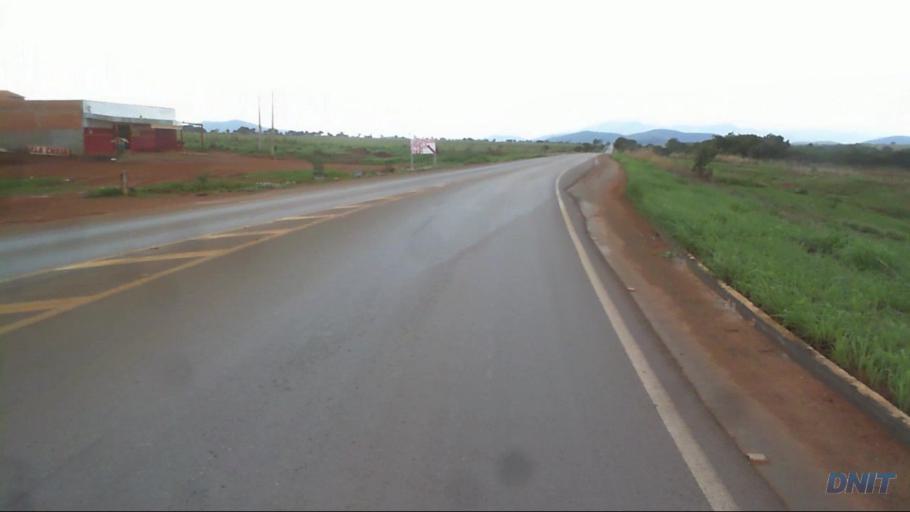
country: BR
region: Goias
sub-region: Barro Alto
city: Barro Alto
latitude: -14.8392
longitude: -49.0307
